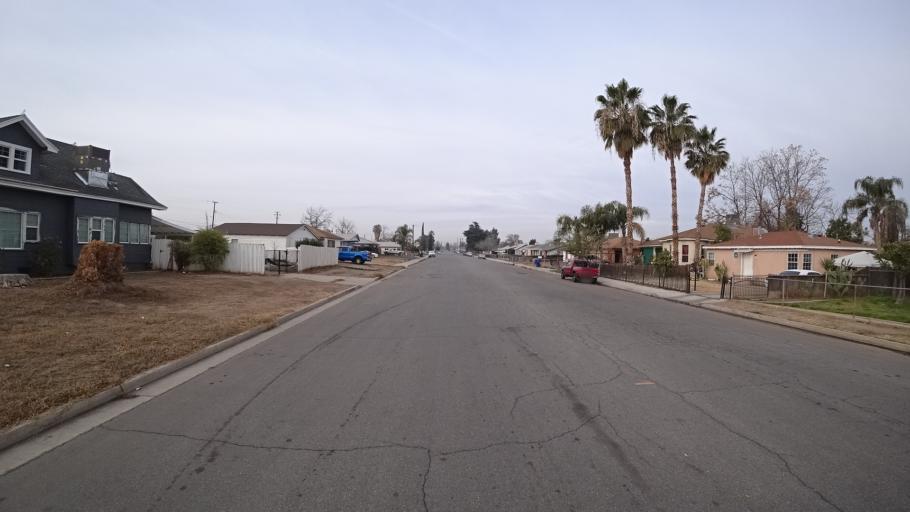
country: US
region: California
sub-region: Kern County
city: Bakersfield
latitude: 35.3570
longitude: -119.0144
